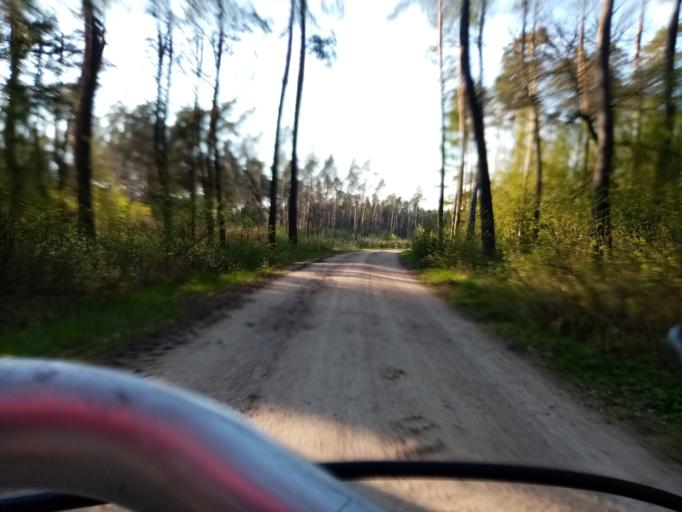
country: PL
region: Kujawsko-Pomorskie
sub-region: Powiat brodnicki
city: Gorzno
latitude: 53.1628
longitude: 19.6785
